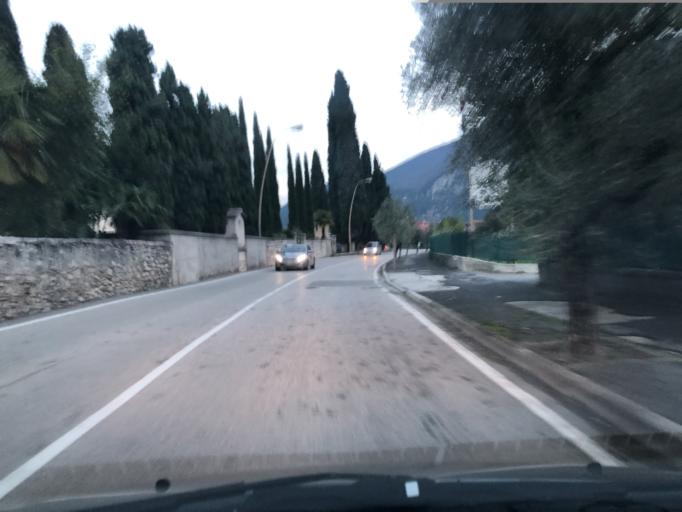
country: IT
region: Trentino-Alto Adige
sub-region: Provincia di Trento
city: Arco
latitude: 45.9107
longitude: 10.8799
